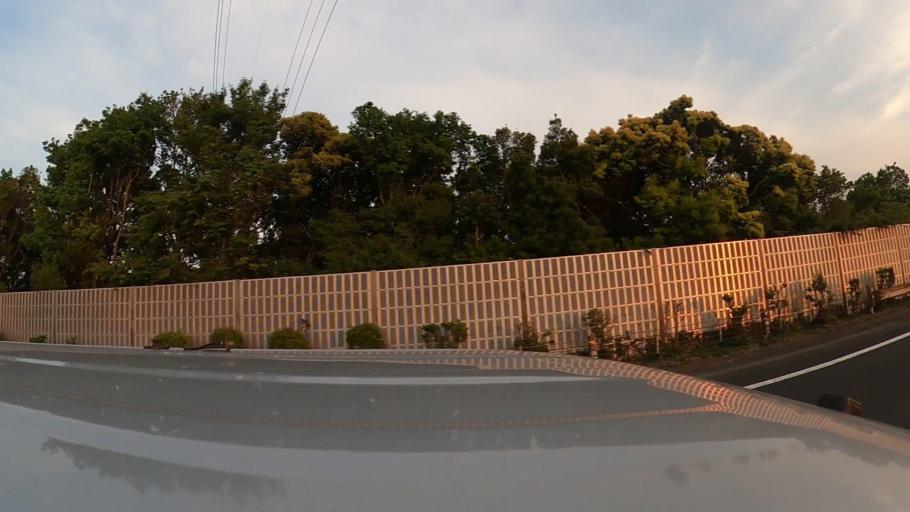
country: JP
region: Ibaraki
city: Mitsukaido
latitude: 35.9866
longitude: 140.0229
